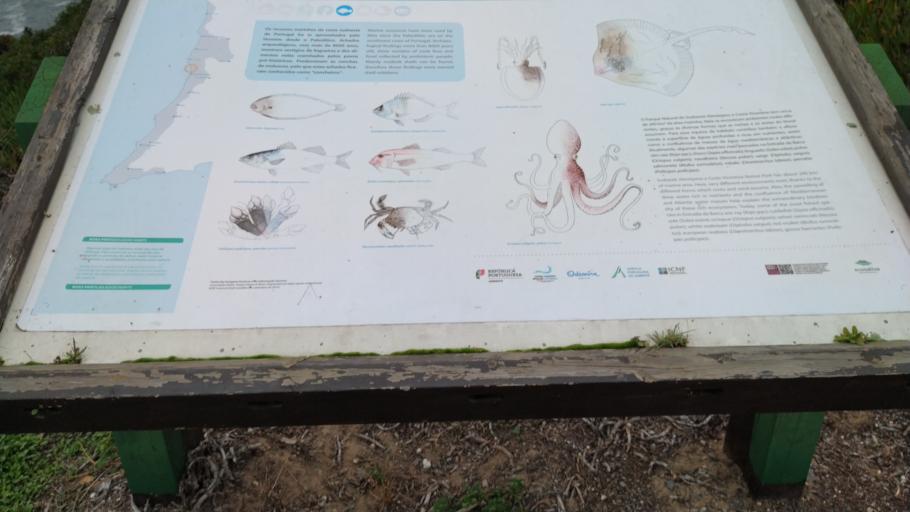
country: PT
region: Beja
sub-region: Odemira
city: Sao Teotonio
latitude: 37.5511
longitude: -8.7915
